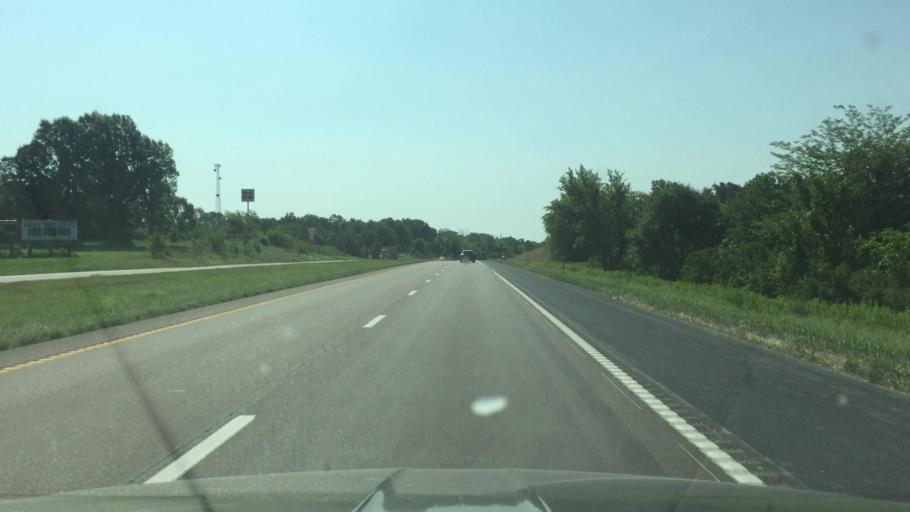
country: US
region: Missouri
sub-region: Pettis County
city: Sedalia
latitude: 38.7366
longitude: -93.3149
